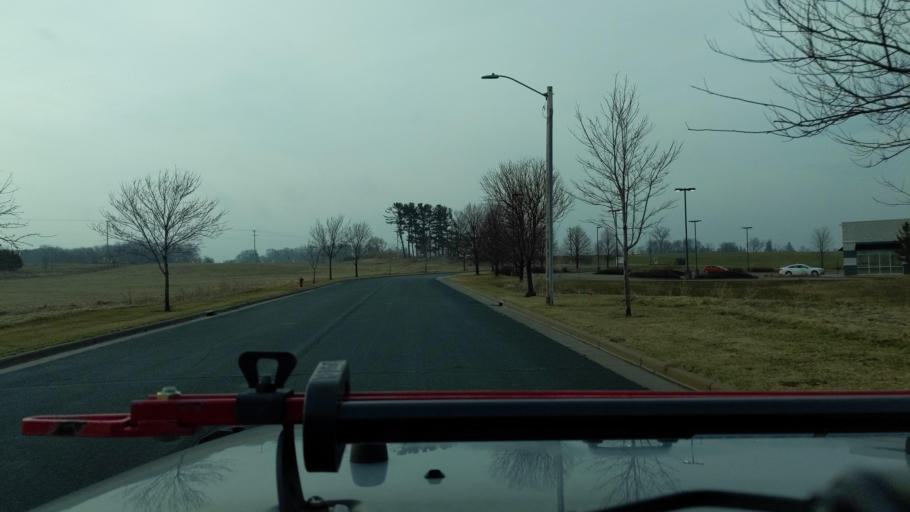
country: US
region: Wisconsin
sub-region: Saint Croix County
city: Baldwin
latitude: 44.9361
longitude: -92.3780
